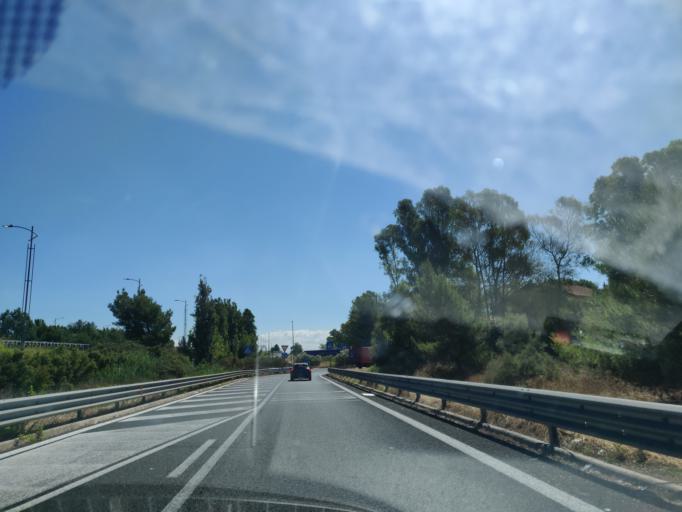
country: IT
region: Latium
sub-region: Citta metropolitana di Roma Capitale
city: Npp 23 (Parco Leonardo)
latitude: 41.8114
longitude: 12.3185
